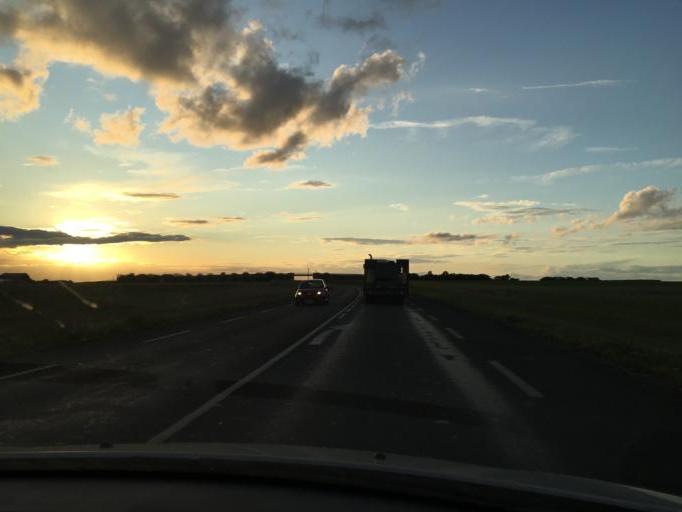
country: FR
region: Centre
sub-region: Departement d'Eure-et-Loir
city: Chateaudun
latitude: 48.0932
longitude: 1.3523
